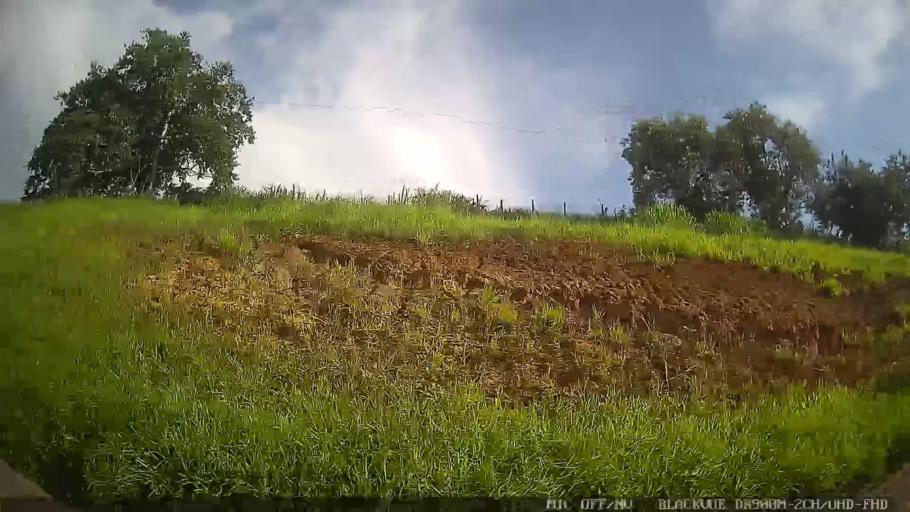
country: BR
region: Sao Paulo
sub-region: Tiete
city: Tiete
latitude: -23.0861
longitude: -47.6771
